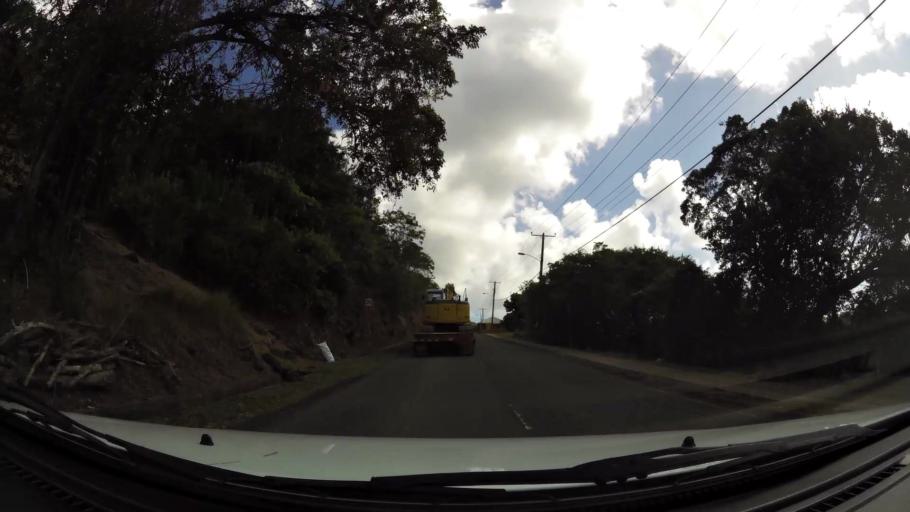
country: LC
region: Laborie Quarter
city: Laborie
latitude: 13.7538
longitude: -60.9991
